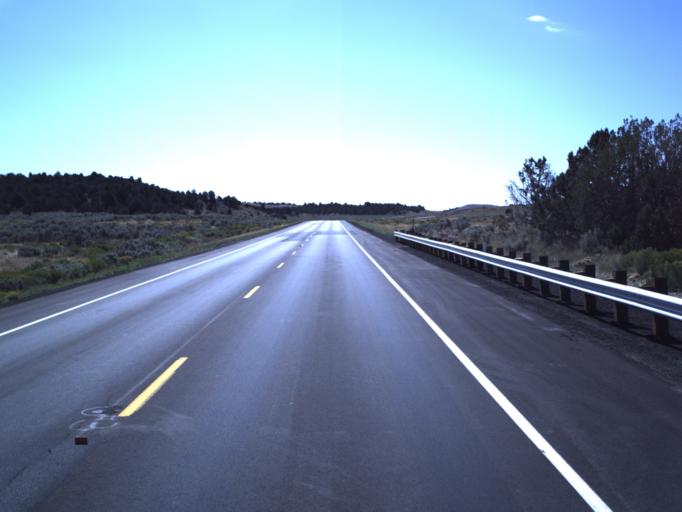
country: US
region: Utah
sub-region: Utah County
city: Eagle Mountain
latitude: 39.9876
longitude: -112.2652
